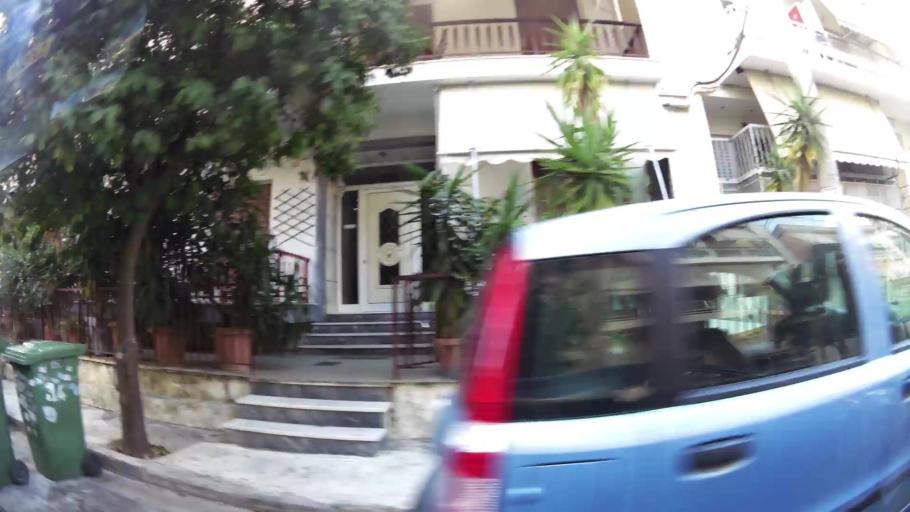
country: GR
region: Attica
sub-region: Nomos Piraios
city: Agios Ioannis Rentis
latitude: 37.9718
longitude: 23.6606
